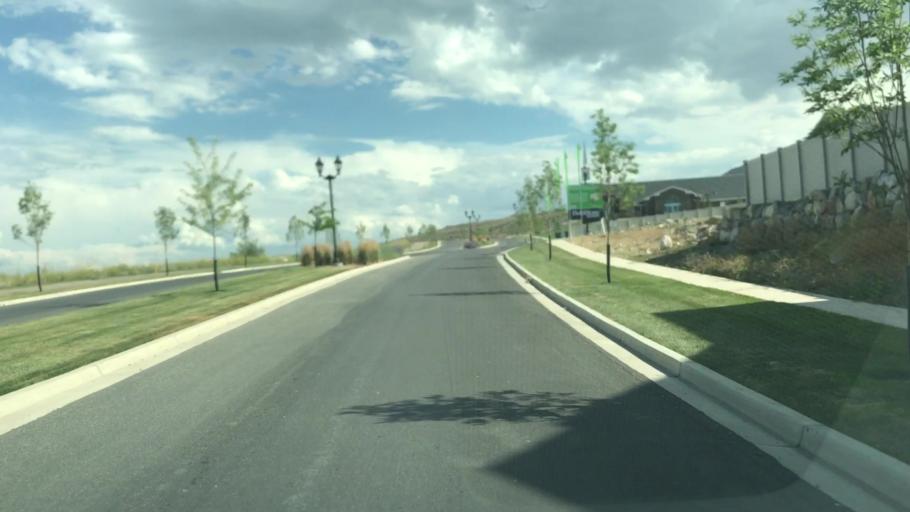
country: US
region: Utah
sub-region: Utah County
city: Saratoga Springs
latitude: 40.3045
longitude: -111.8994
